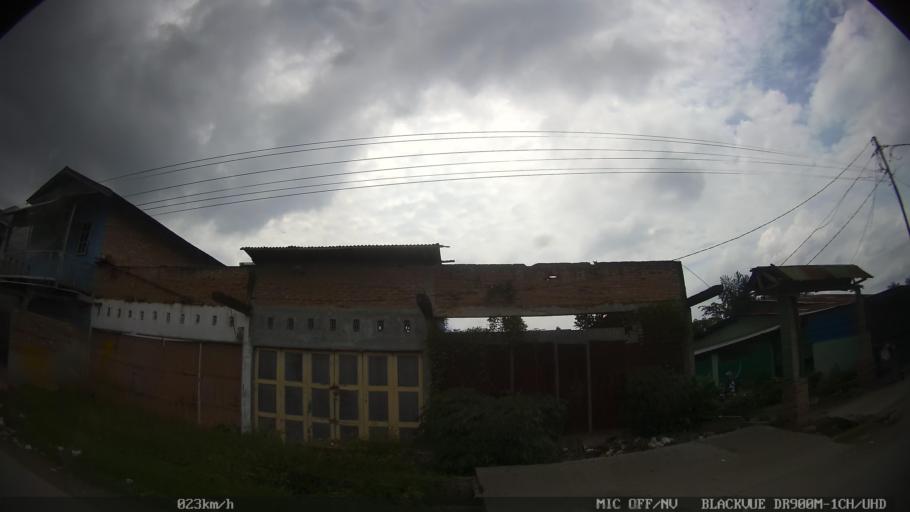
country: ID
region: North Sumatra
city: Sunggal
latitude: 3.6219
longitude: 98.6058
